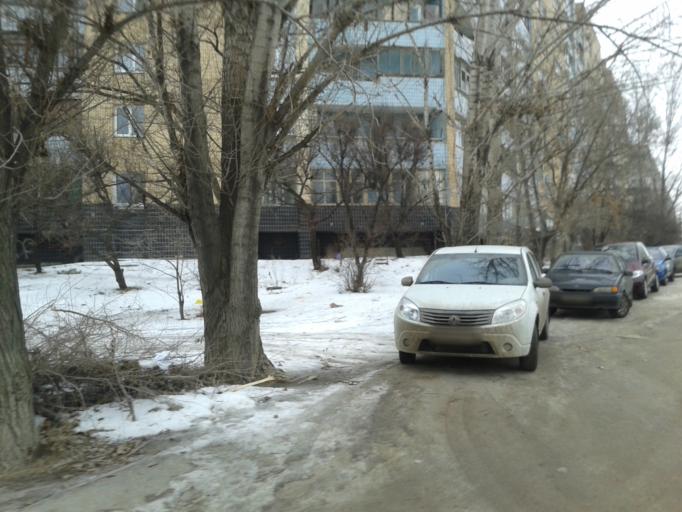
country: RU
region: Volgograd
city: Volgograd
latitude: 48.7260
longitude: 44.5241
